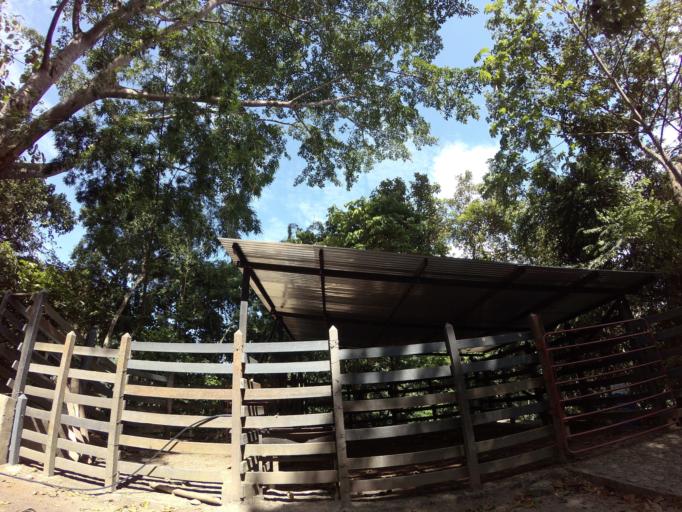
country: CO
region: Caldas
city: Norcasia
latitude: 5.5650
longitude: -74.9073
